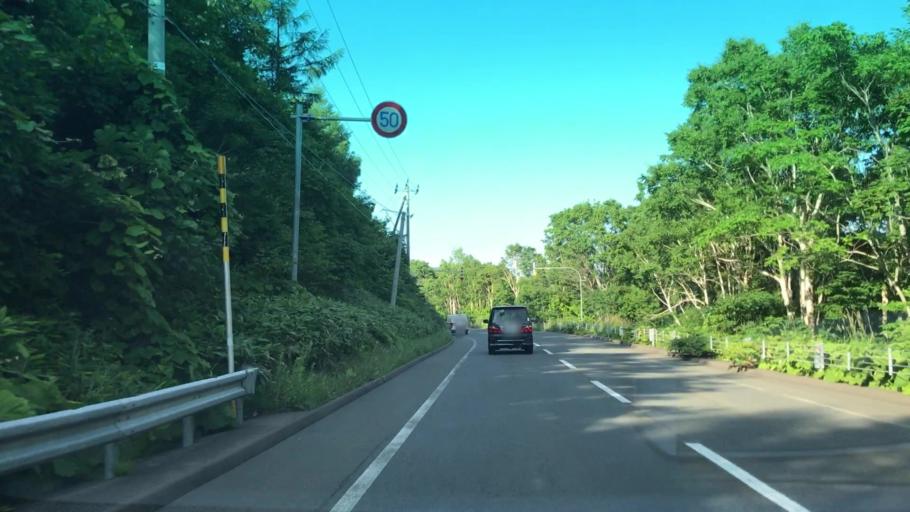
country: JP
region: Hokkaido
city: Otaru
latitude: 43.1100
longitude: 141.0064
